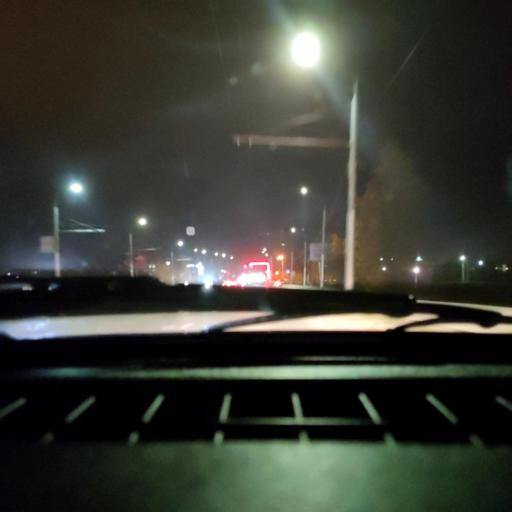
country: RU
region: Bashkortostan
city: Ufa
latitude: 54.7902
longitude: 56.0780
